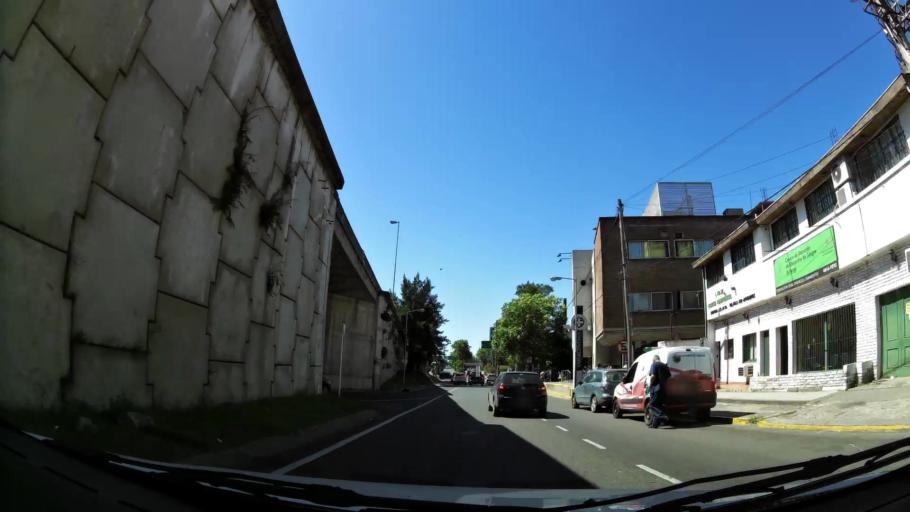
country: AR
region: Buenos Aires
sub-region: Partido de Vicente Lopez
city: Olivos
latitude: -34.5184
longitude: -58.5164
